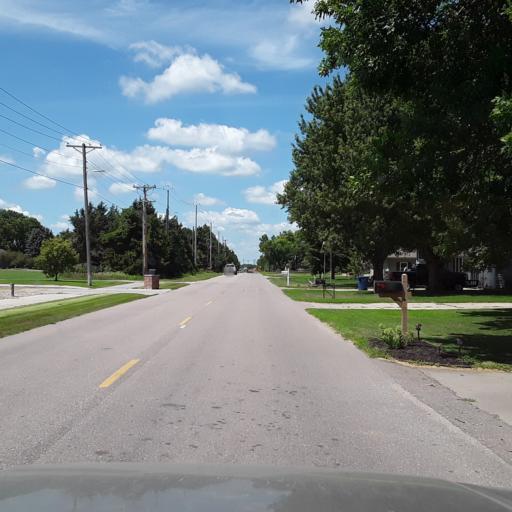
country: US
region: Nebraska
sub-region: Merrick County
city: Central City
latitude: 41.1048
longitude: -98.0117
